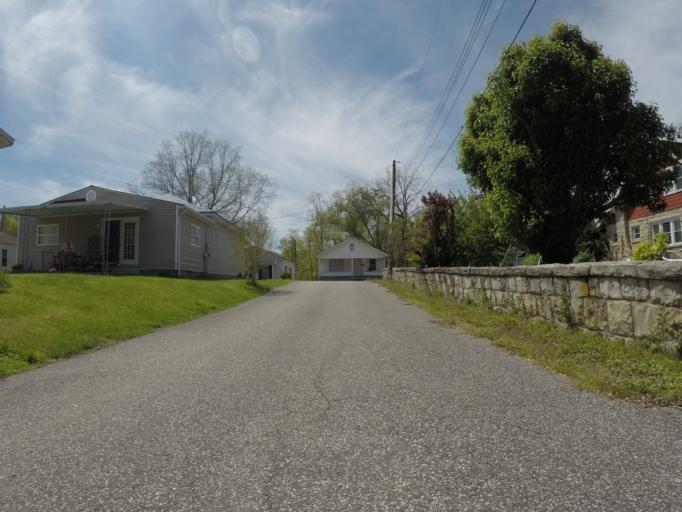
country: US
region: Kentucky
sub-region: Boyd County
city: Catlettsburg
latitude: 38.4006
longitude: -82.5977
